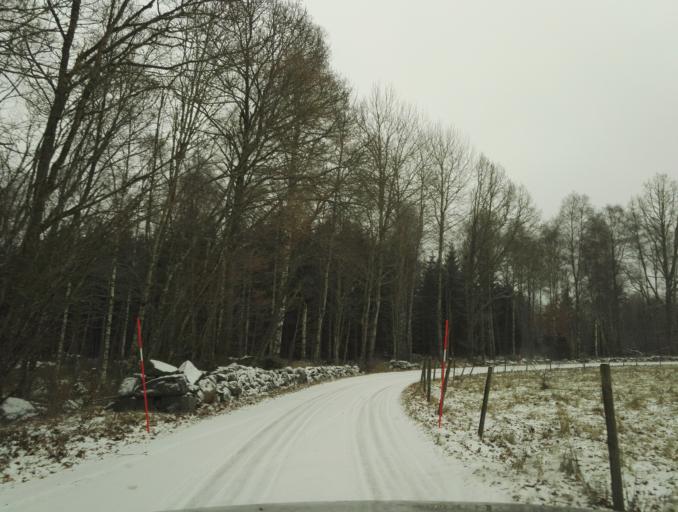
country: SE
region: Kronoberg
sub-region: Alvesta Kommun
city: Vislanda
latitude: 56.6958
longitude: 14.4174
